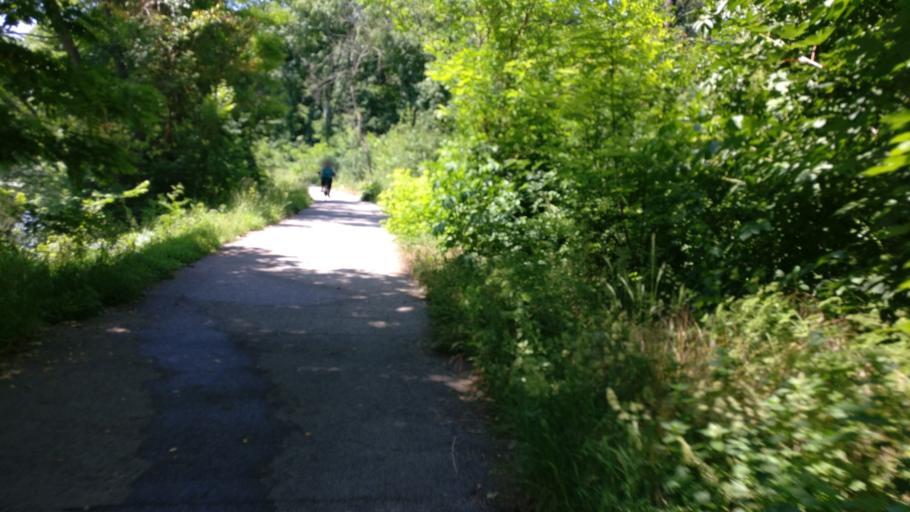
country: AT
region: Lower Austria
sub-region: Politischer Bezirk Baden
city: Oberwaltersdorf
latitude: 47.9717
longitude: 16.3174
